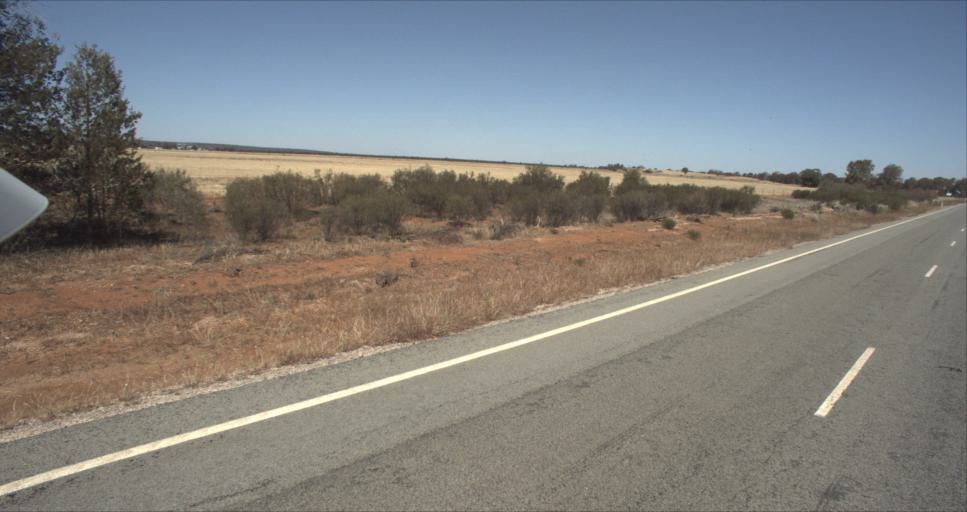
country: AU
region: New South Wales
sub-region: Leeton
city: Leeton
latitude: -34.4899
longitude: 146.4326
